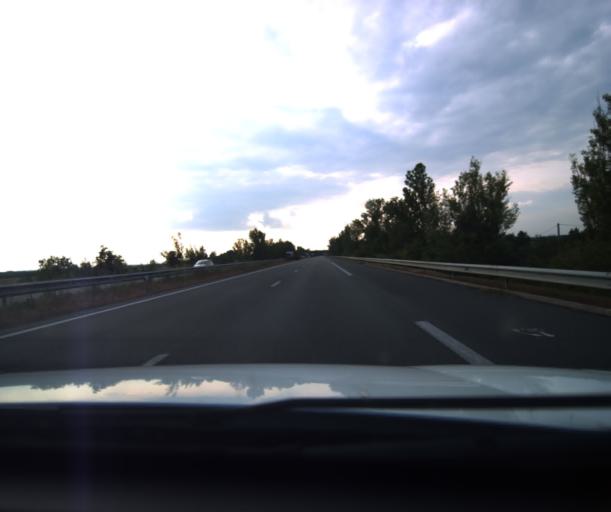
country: FR
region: Midi-Pyrenees
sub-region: Departement du Tarn-et-Garonne
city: Montech
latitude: 43.9826
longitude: 1.2504
